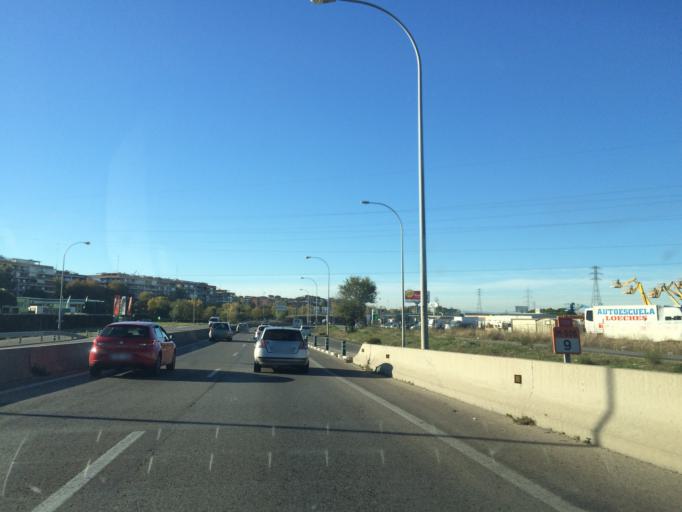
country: ES
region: Madrid
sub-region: Provincia de Madrid
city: Mostoles
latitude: 40.3250
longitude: -3.8451
